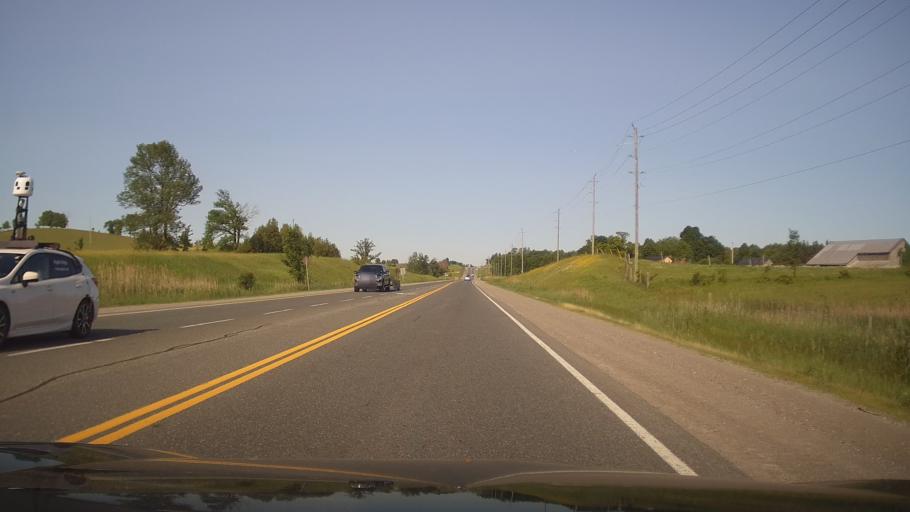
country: CA
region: Ontario
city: Peterborough
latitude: 44.3337
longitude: -78.1191
